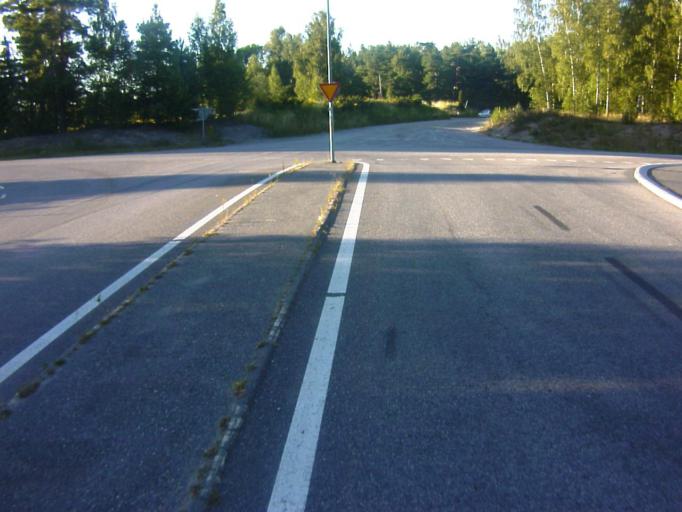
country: SE
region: Soedermanland
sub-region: Eskilstuna Kommun
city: Hallbybrunn
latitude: 59.4000
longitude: 16.4105
